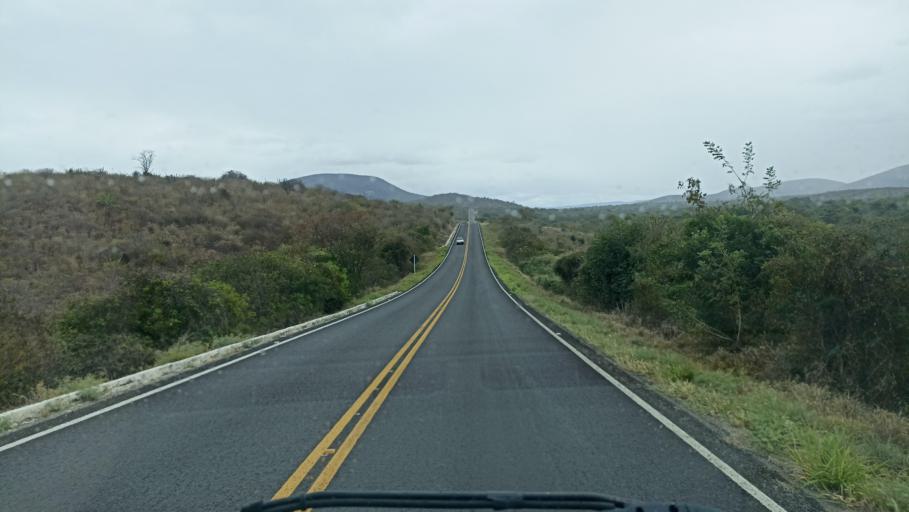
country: BR
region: Bahia
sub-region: Andarai
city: Vera Cruz
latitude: -13.0493
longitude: -40.7546
